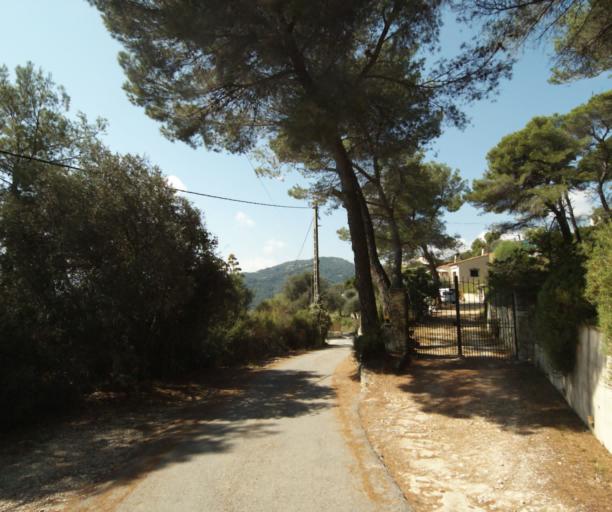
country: FR
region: Provence-Alpes-Cote d'Azur
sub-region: Departement des Alpes-Maritimes
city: Drap
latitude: 43.7591
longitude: 7.3303
